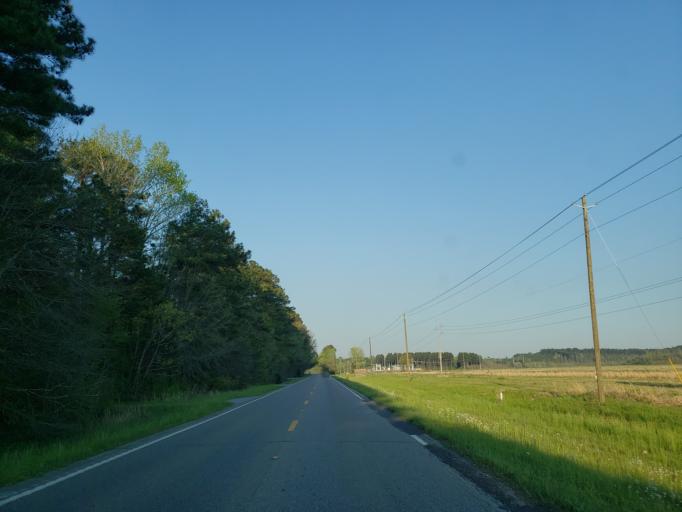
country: US
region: Mississippi
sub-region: Lauderdale County
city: Marion
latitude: 32.3946
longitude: -88.6248
